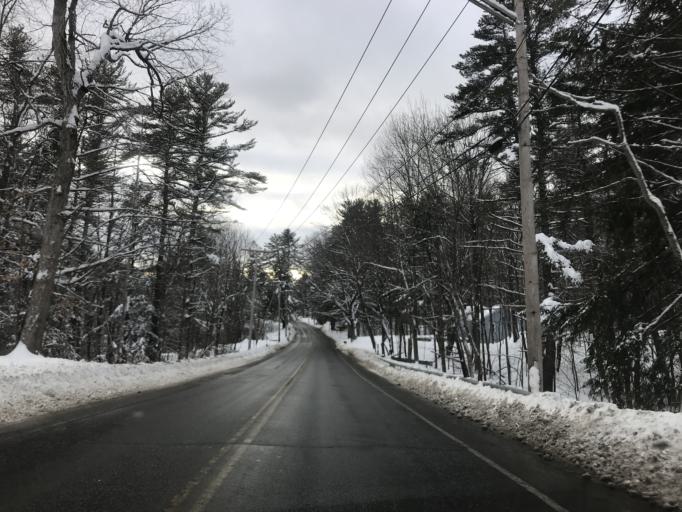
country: US
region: Maine
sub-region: Cumberland County
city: Falmouth
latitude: 43.7261
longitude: -70.3145
